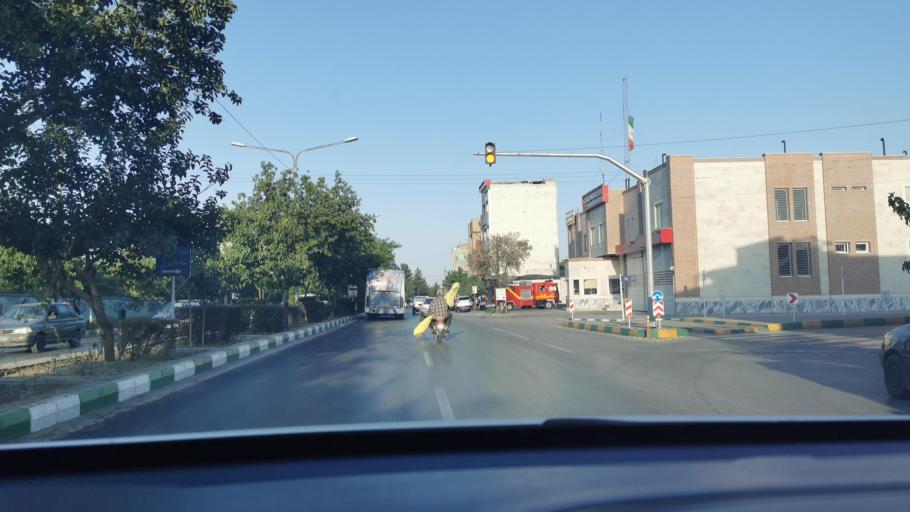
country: IR
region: Razavi Khorasan
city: Mashhad
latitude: 36.2888
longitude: 59.6555
